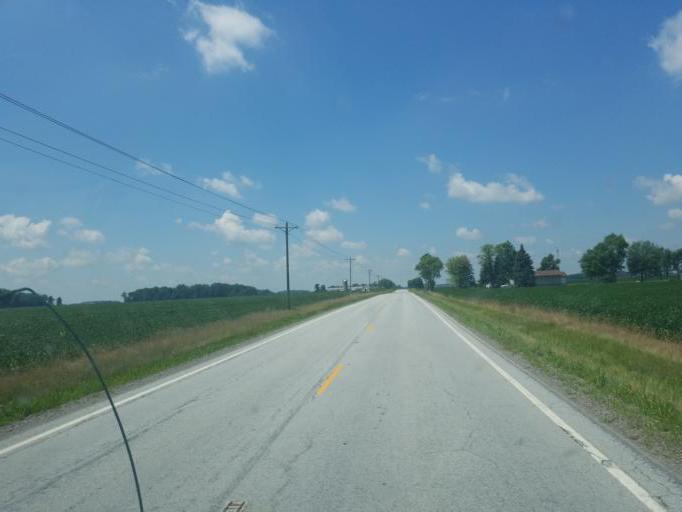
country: US
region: Ohio
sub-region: Allen County
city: Spencerville
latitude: 40.7141
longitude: -84.4002
